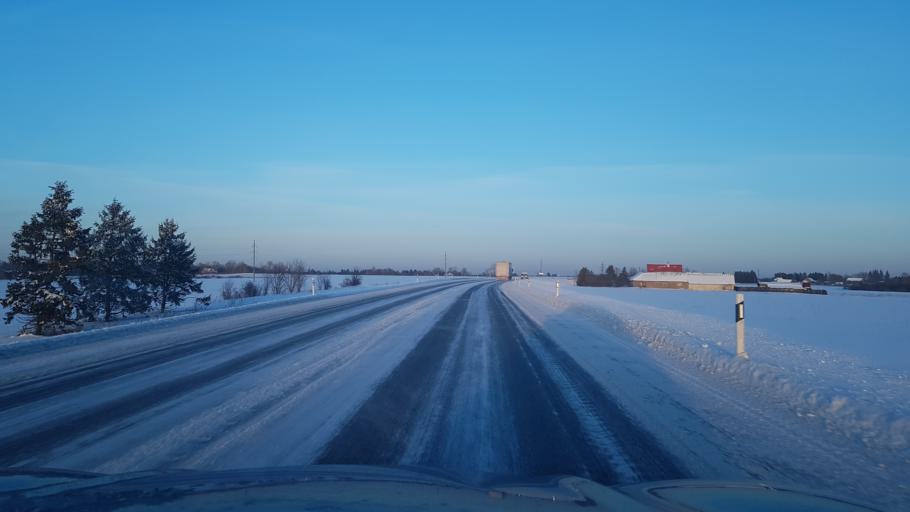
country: EE
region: Ida-Virumaa
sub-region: Narva-Joesuu linn
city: Narva-Joesuu
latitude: 59.4022
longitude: 28.0153
